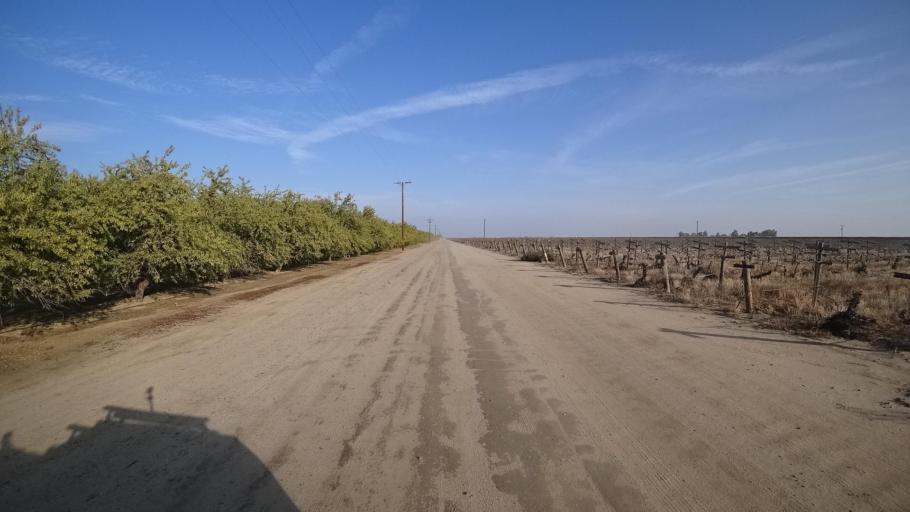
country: US
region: California
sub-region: Kern County
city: Delano
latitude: 35.7348
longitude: -119.1873
